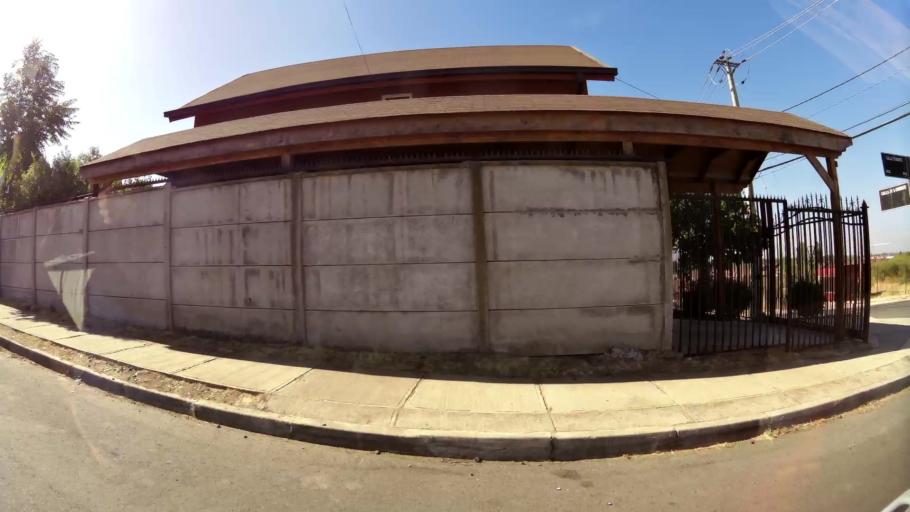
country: CL
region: Maule
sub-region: Provincia de Talca
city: Talca
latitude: -35.4209
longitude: -71.6168
